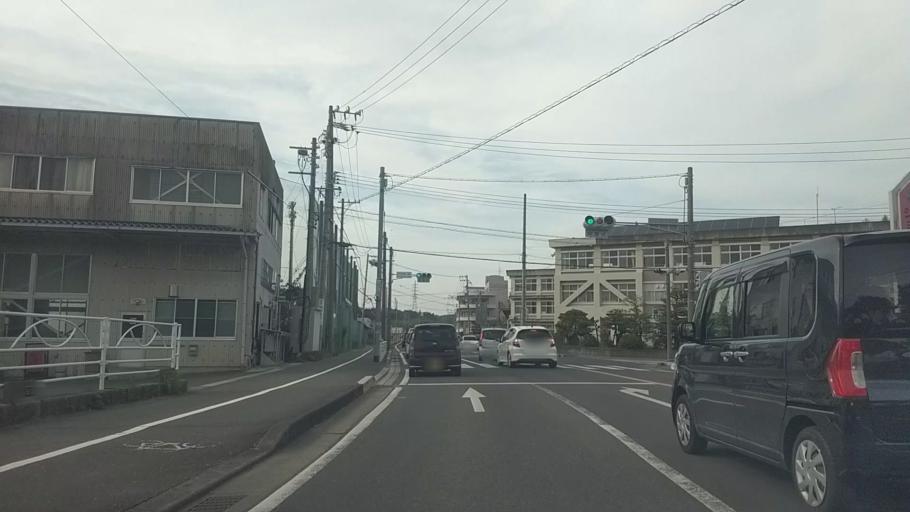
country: JP
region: Shizuoka
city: Hamamatsu
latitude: 34.7443
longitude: 137.6551
